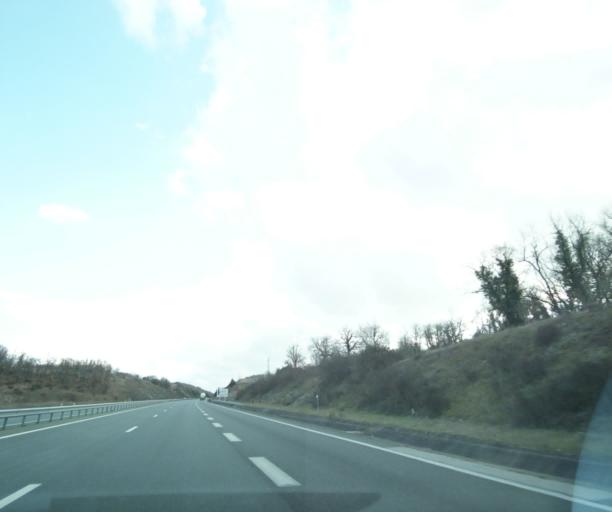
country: FR
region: Midi-Pyrenees
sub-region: Departement du Lot
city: Le Vigan
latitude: 44.7187
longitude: 1.5654
